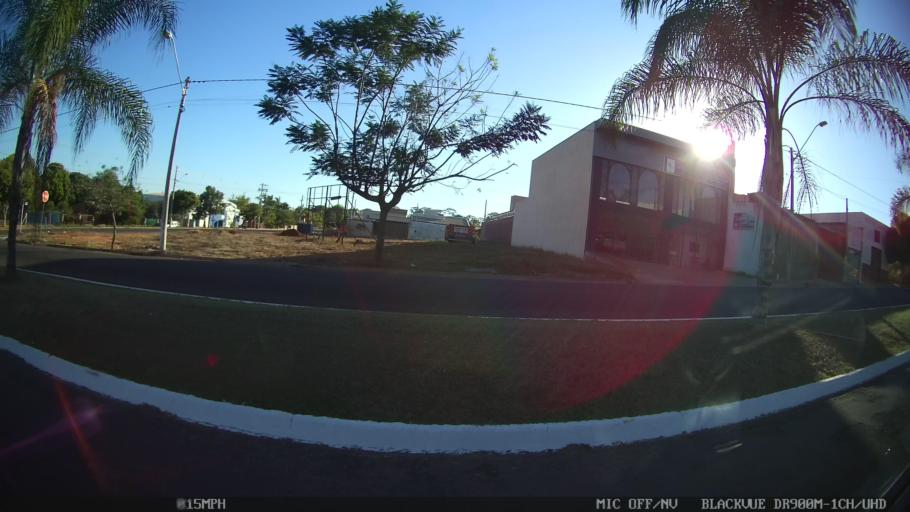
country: BR
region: Sao Paulo
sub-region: Guapiacu
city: Guapiacu
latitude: -20.7920
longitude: -49.2361
